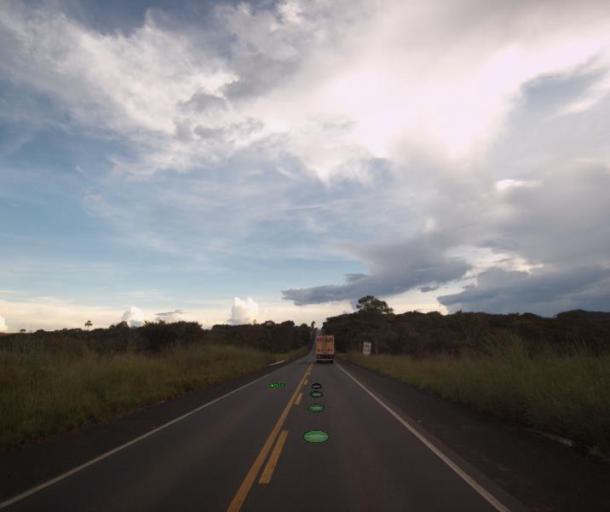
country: BR
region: Goias
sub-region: Uruacu
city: Uruacu
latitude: -14.1488
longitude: -49.1183
